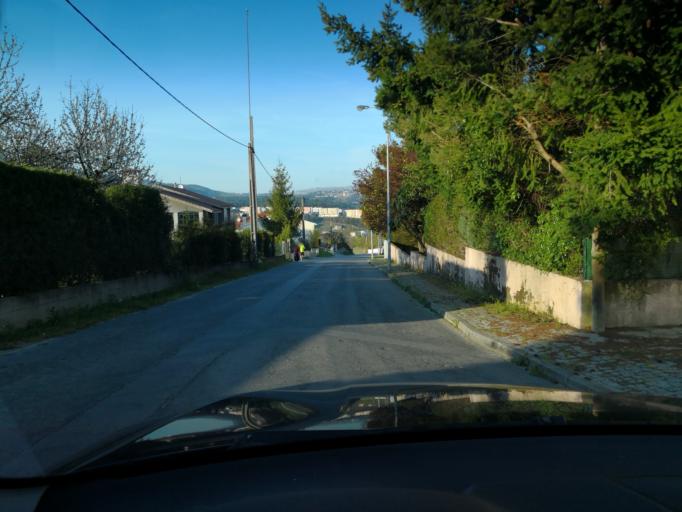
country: PT
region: Vila Real
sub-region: Vila Real
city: Vila Real
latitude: 41.2982
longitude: -7.7655
